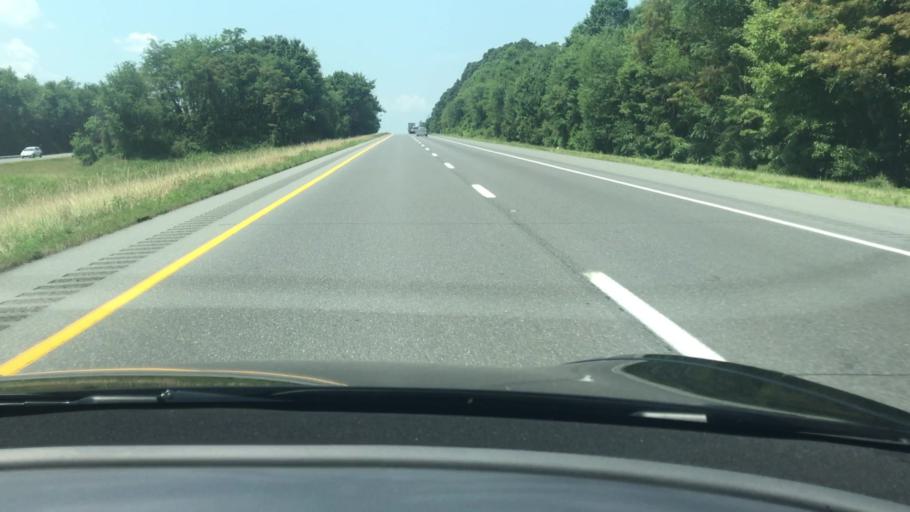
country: US
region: Pennsylvania
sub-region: Juniata County
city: Mifflintown
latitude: 40.5585
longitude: -77.2822
